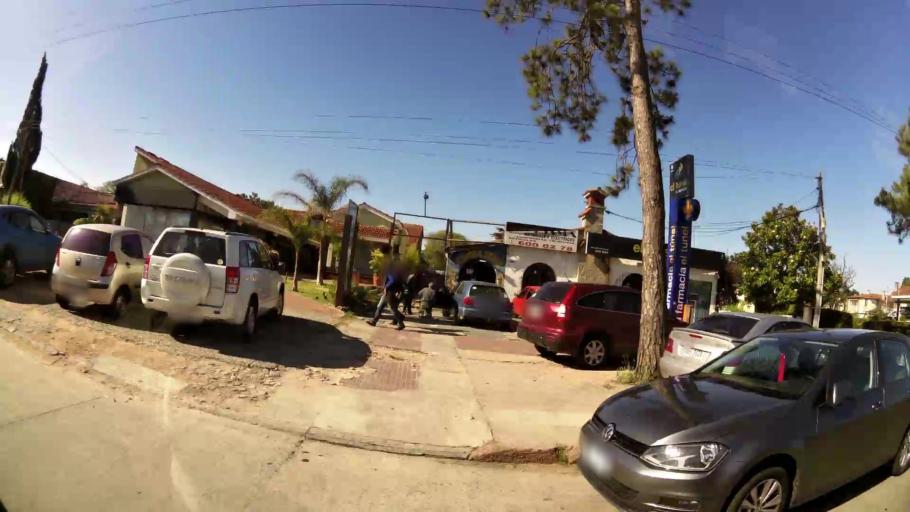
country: UY
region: Canelones
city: Paso de Carrasco
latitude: -34.8798
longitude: -56.0638
